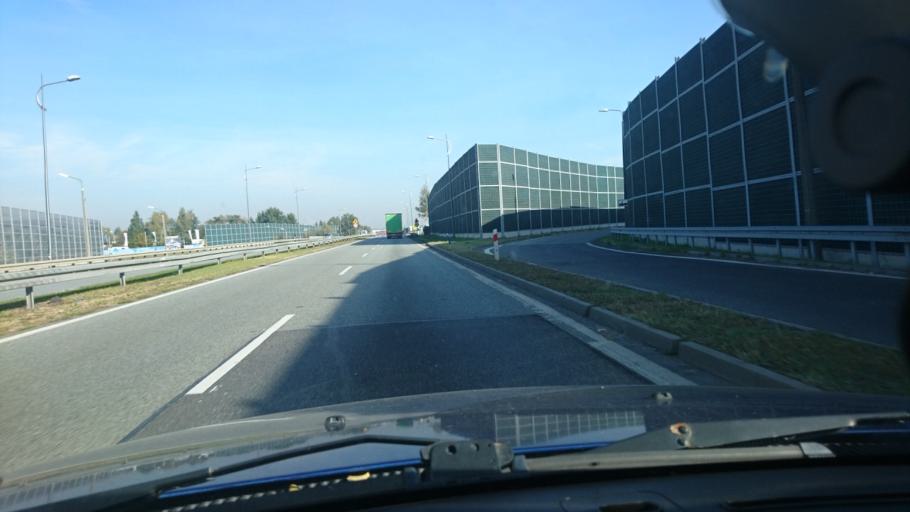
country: PL
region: Silesian Voivodeship
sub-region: Tychy
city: Cielmice
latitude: 50.0852
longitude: 19.0040
